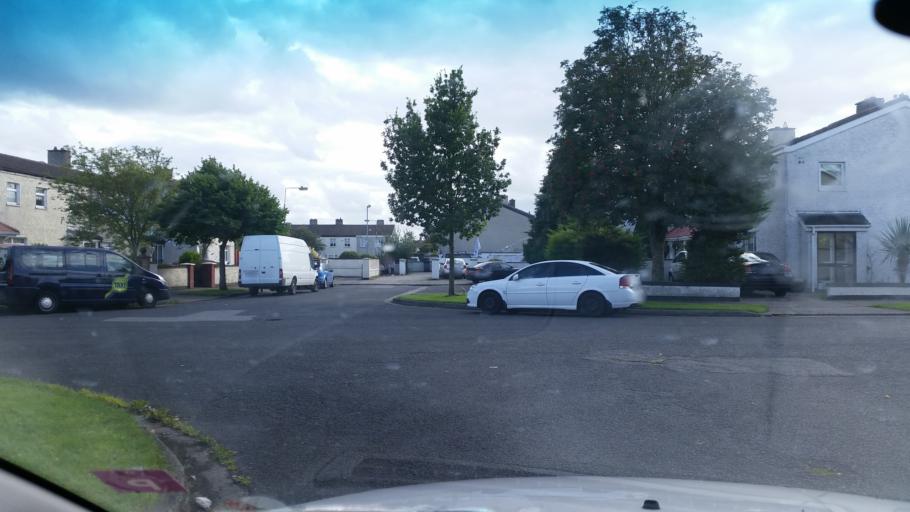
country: IE
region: Leinster
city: Ballymun
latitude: 53.3968
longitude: -6.2545
